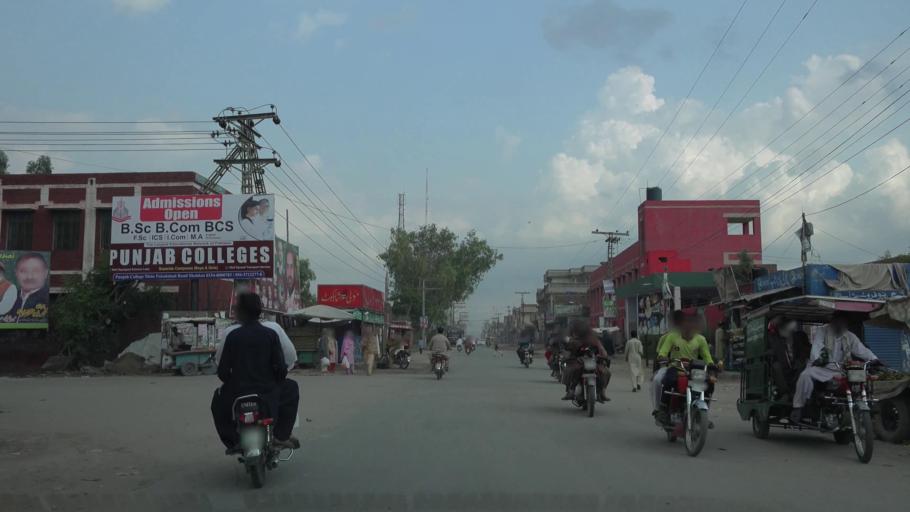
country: PK
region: Punjab
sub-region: Nankana Sahib District
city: Shahkot
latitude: 31.5729
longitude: 73.4854
